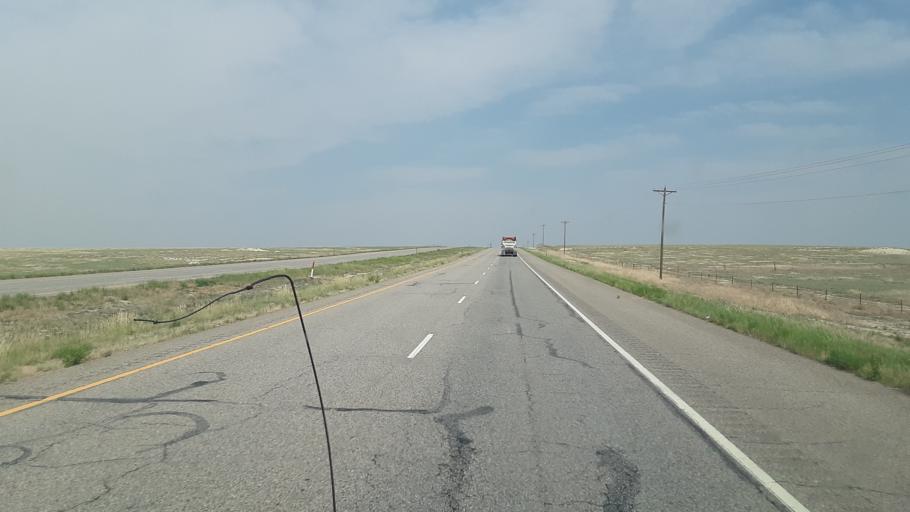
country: US
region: Colorado
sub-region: Fremont County
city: Penrose
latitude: 38.3654
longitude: -104.9021
